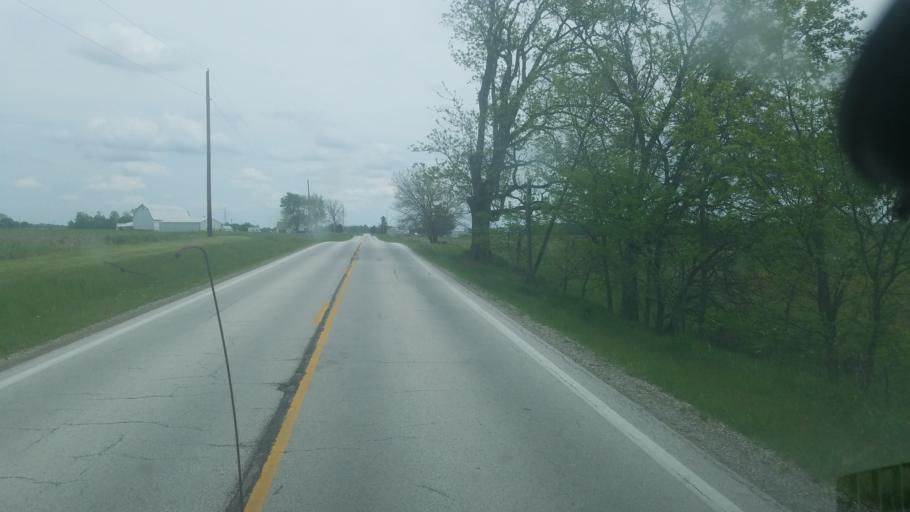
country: US
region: Ohio
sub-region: Seneca County
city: Tiffin
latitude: 41.0416
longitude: -83.1250
